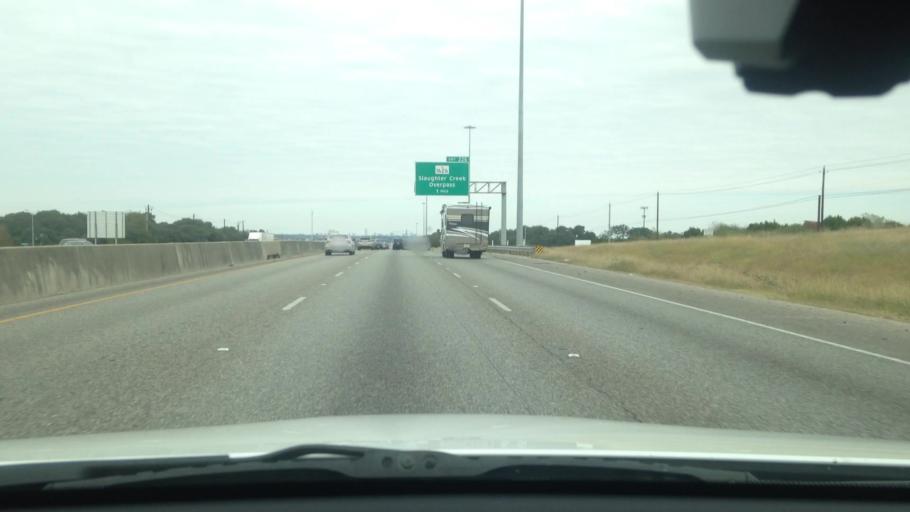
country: US
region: Texas
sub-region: Travis County
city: Onion Creek
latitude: 30.1218
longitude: -97.8028
